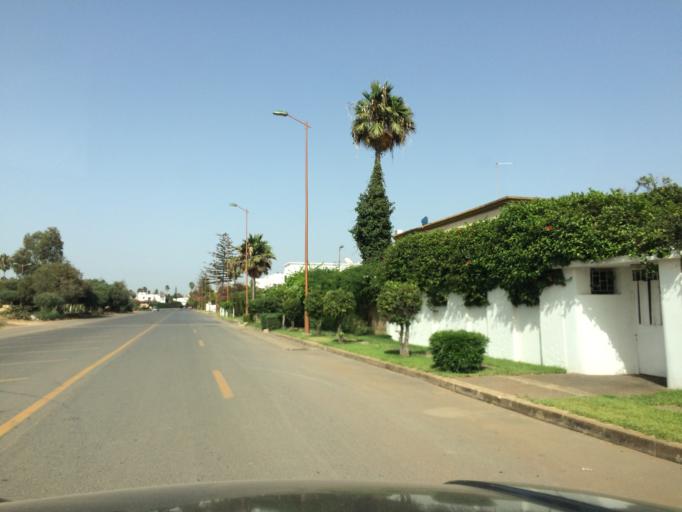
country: MA
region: Rabat-Sale-Zemmour-Zaer
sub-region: Rabat
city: Rabat
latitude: 33.9873
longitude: -6.8374
